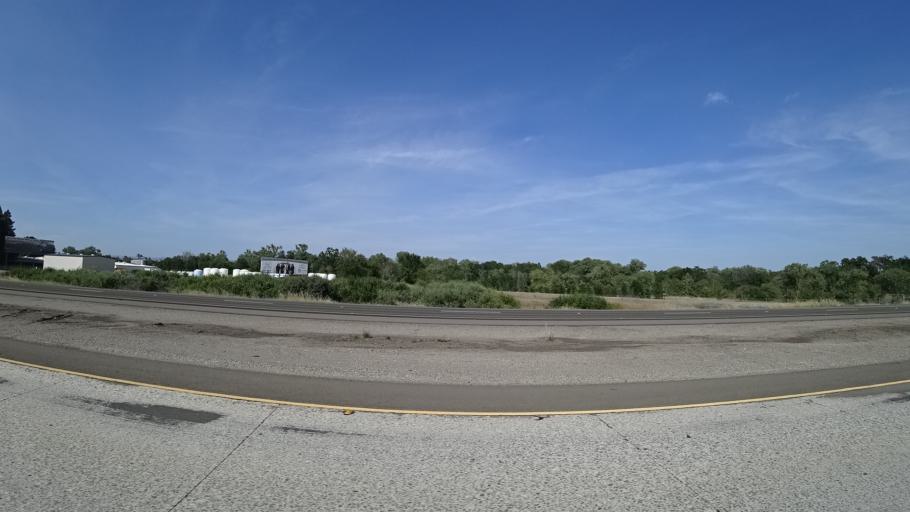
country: US
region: California
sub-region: Butte County
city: Durham
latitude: 39.6955
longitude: -121.7795
